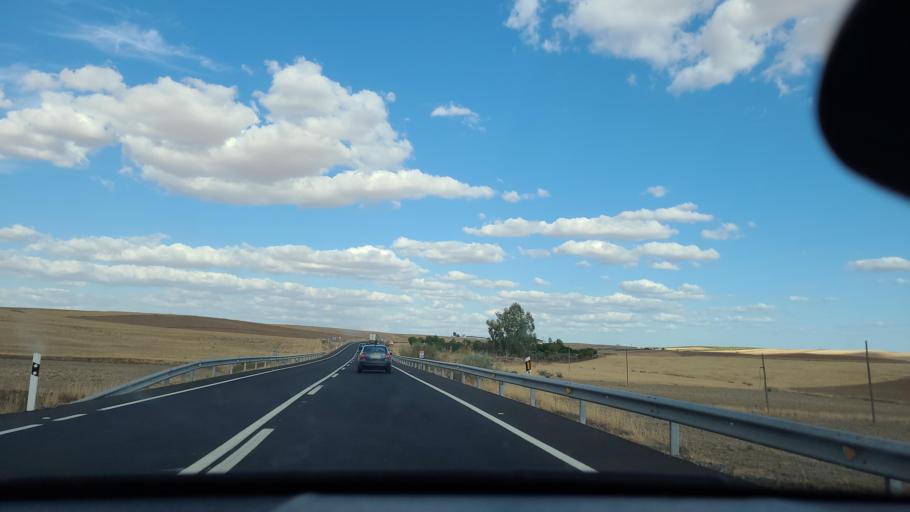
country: ES
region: Extremadura
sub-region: Provincia de Badajoz
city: Berlanga
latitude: 38.2726
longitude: -5.8078
